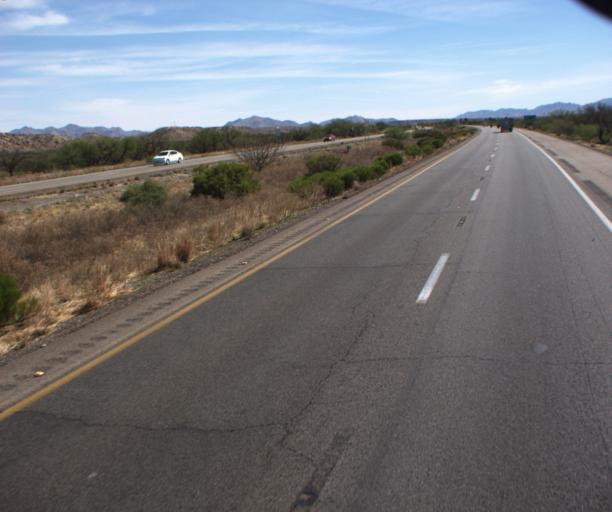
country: US
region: Arizona
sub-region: Cochise County
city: Benson
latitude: 31.9653
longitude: -110.2569
